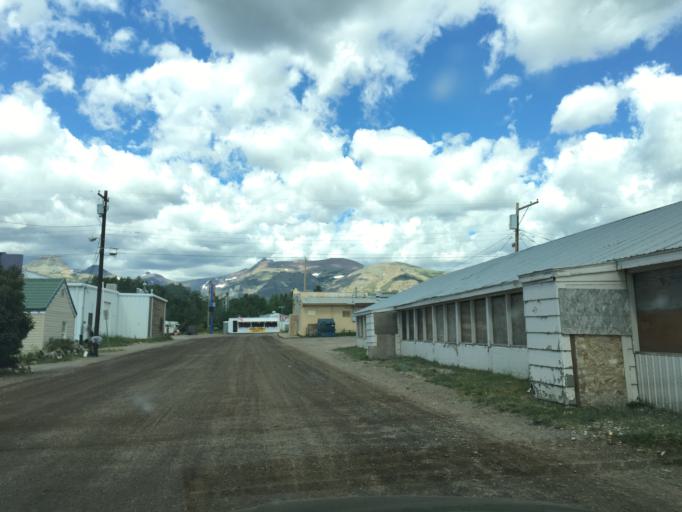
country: US
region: Montana
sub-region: Glacier County
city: South Browning
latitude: 48.4411
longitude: -113.2173
